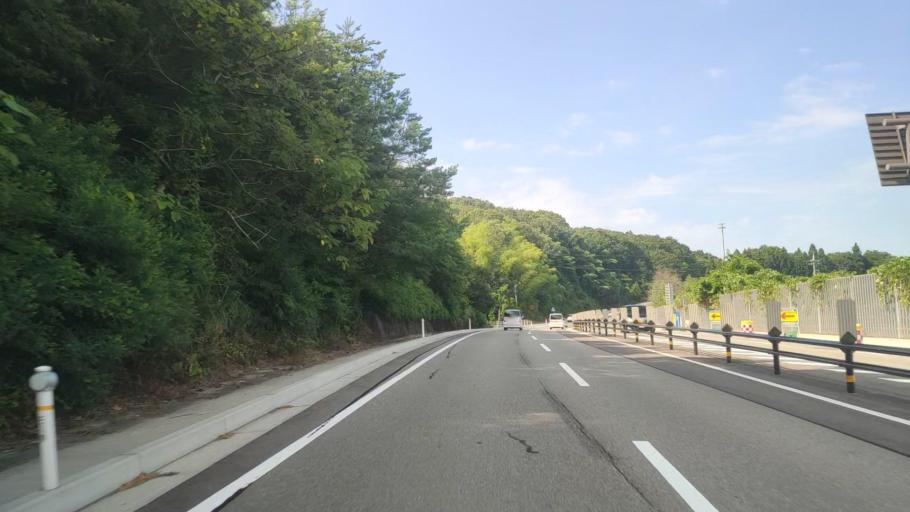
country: JP
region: Ishikawa
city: Matsuto
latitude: 36.4348
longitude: 136.5418
